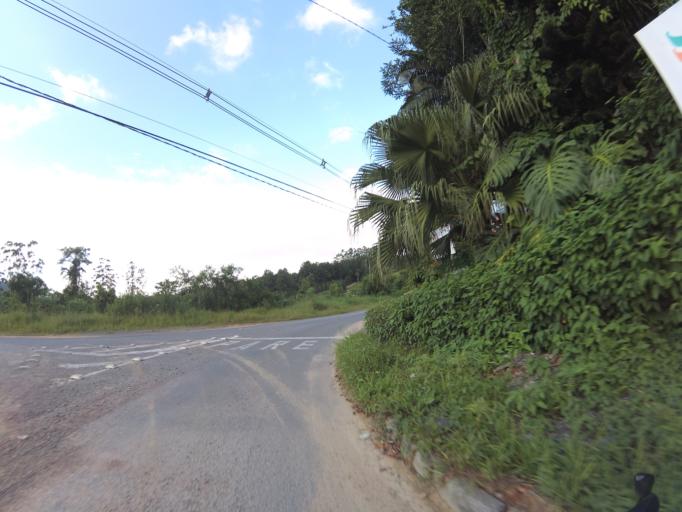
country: BR
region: Santa Catarina
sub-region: Pomerode
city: Pomerode
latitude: -26.8154
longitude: -49.1619
